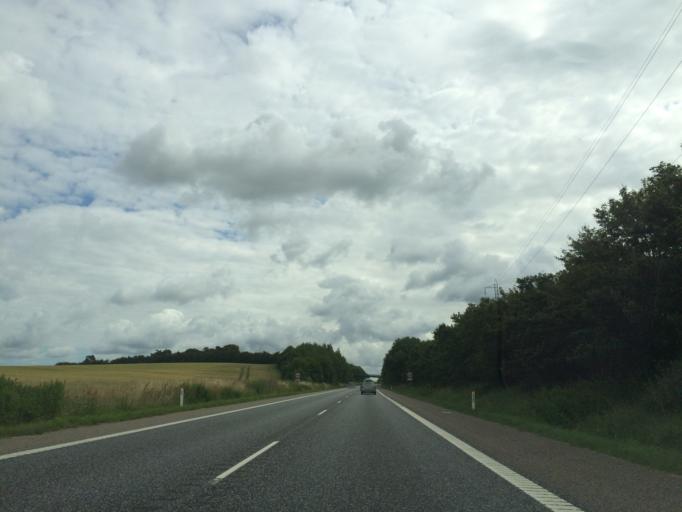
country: DK
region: Central Jutland
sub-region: Syddjurs Kommune
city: Hornslet
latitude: 56.3088
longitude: 10.3687
